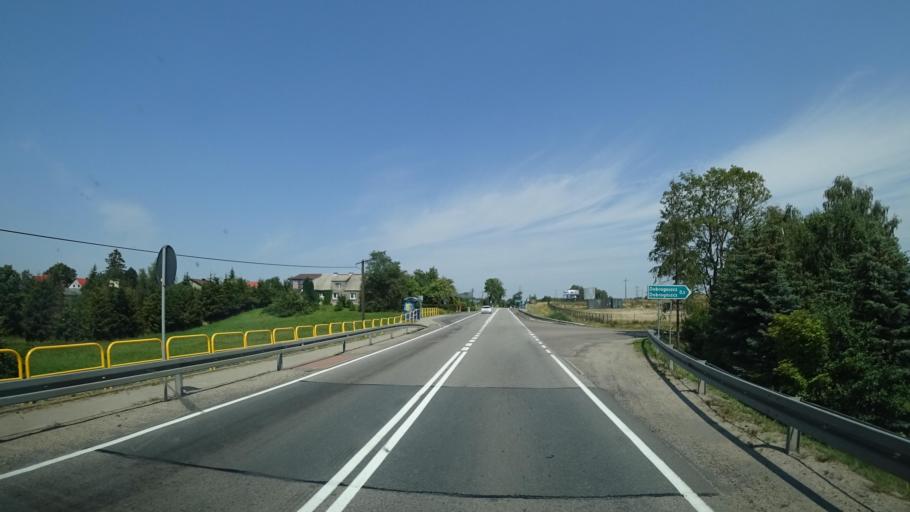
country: PL
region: Pomeranian Voivodeship
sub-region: Powiat koscierski
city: Koscierzyna
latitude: 54.1459
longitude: 18.0254
